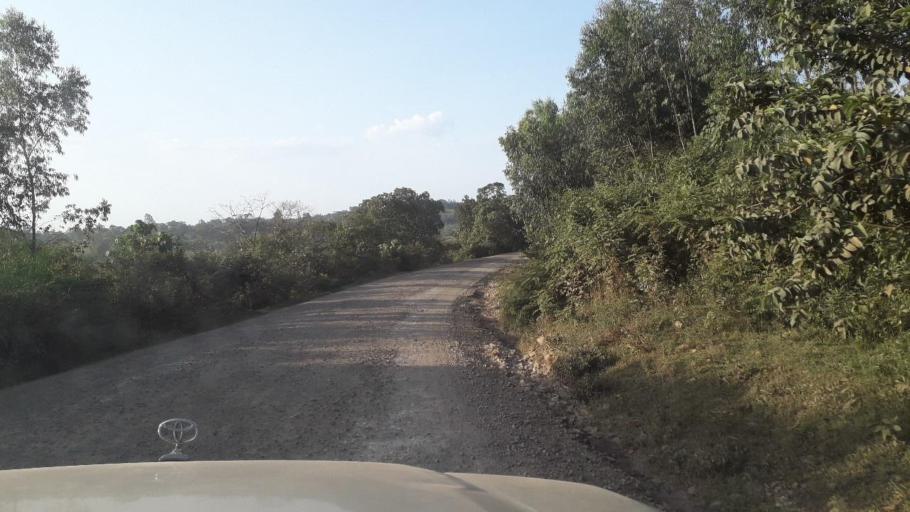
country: ET
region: Oromiya
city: Jima
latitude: 7.5753
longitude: 36.8579
